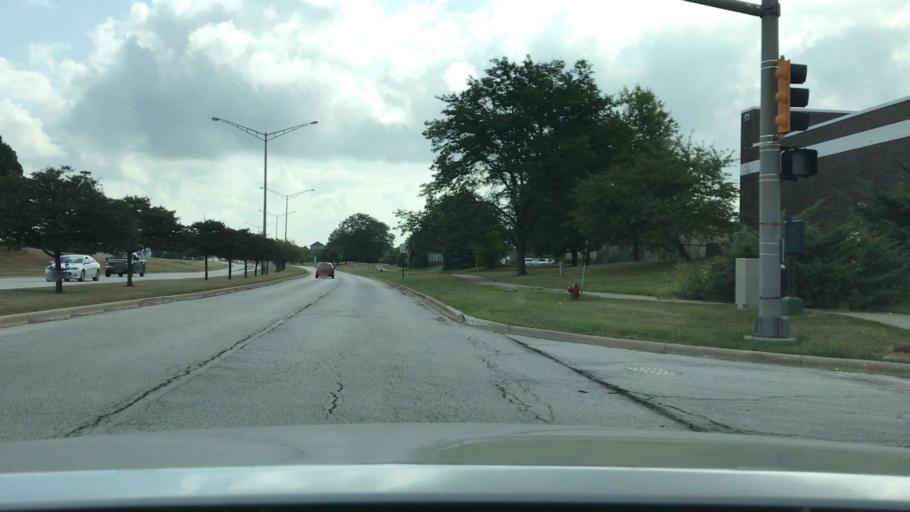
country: US
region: Illinois
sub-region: DuPage County
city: Naperville
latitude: 41.7548
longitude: -88.2144
